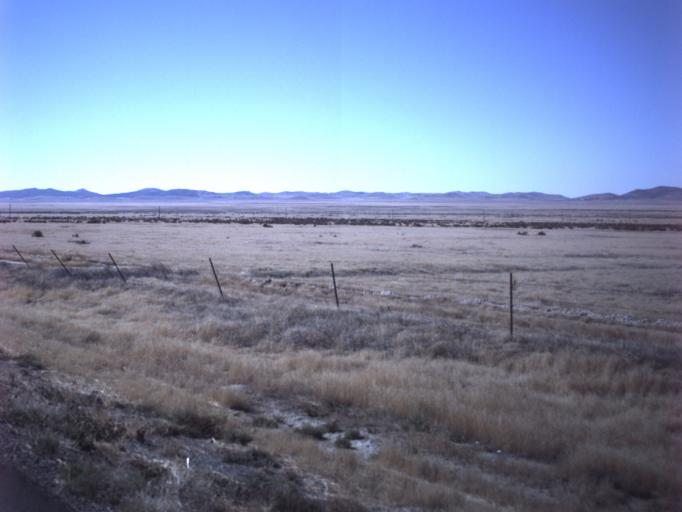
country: US
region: Utah
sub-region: Tooele County
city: Grantsville
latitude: 40.3739
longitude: -112.7466
